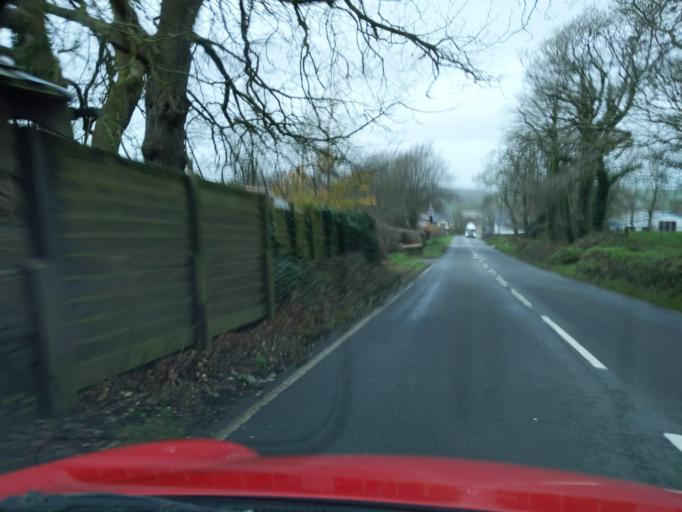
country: GB
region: England
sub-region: Devon
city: Holsworthy
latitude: 50.7656
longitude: -4.3361
